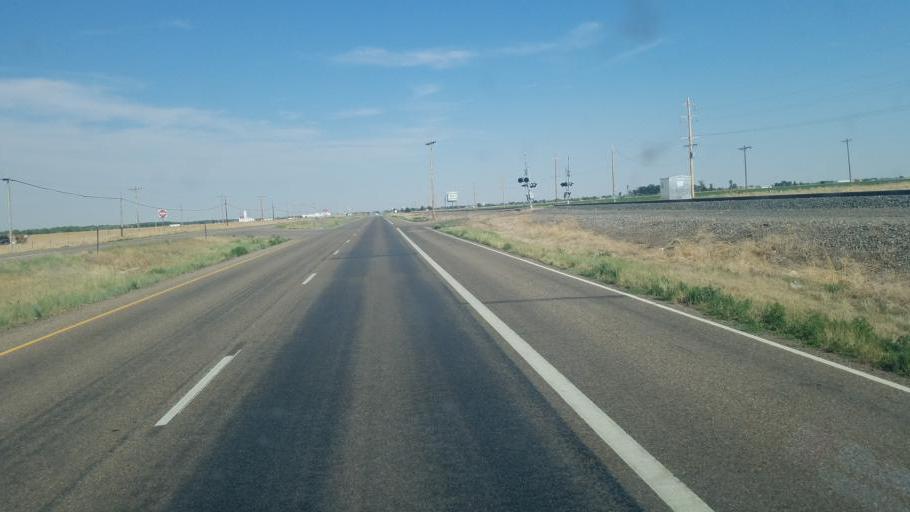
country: US
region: Colorado
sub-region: Otero County
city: Rocky Ford
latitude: 38.0349
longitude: -103.6750
